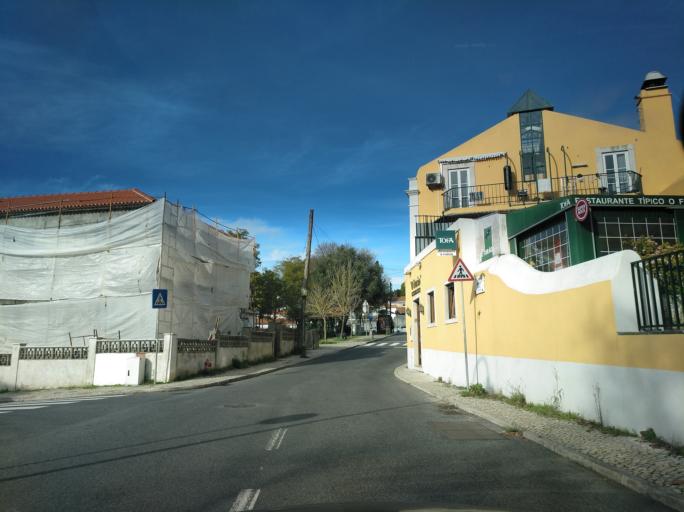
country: PT
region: Lisbon
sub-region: Oeiras
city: Alges
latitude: 38.7152
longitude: -9.2147
